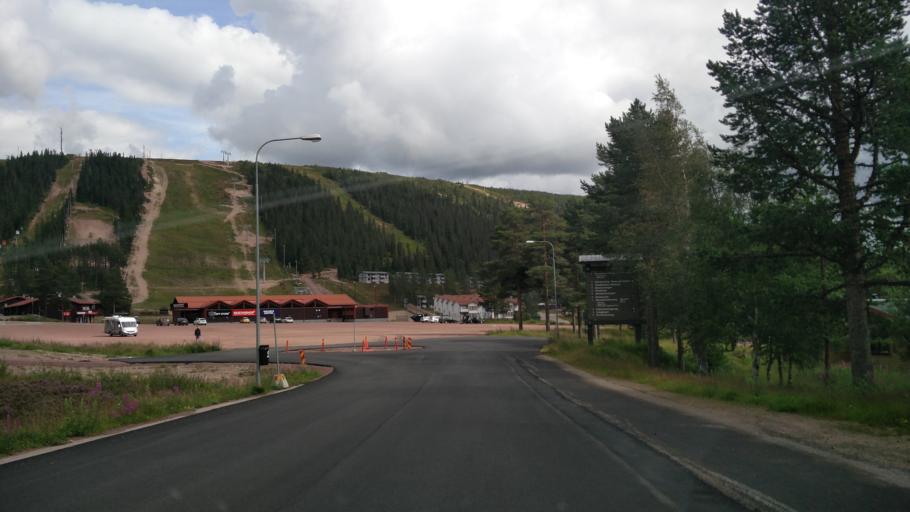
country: NO
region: Hedmark
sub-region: Trysil
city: Innbygda
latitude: 61.1755
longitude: 12.9947
